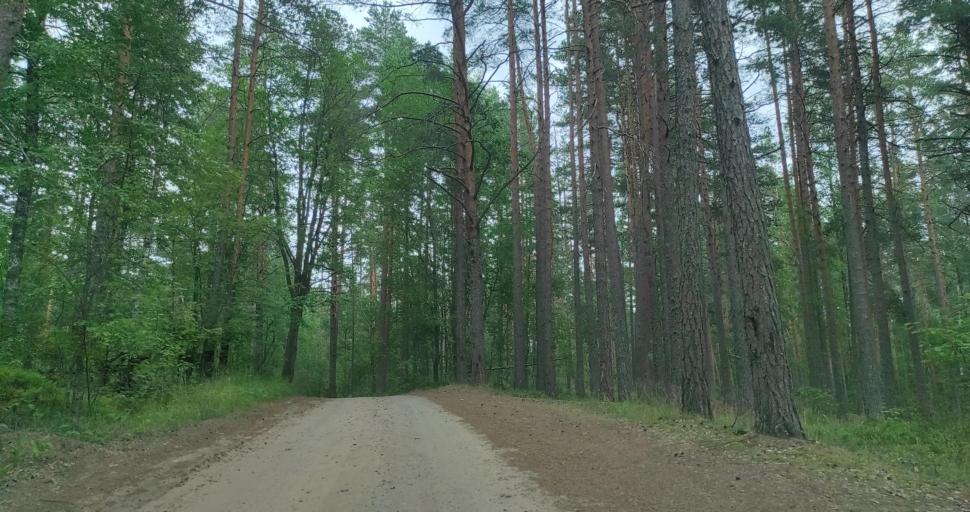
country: RU
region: Leningrad
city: Sapernoye
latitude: 60.6796
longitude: 29.9723
